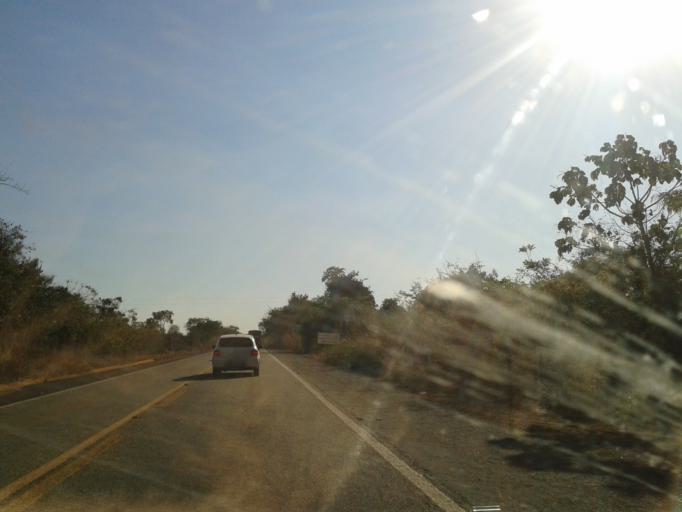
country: BR
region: Goias
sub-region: Mozarlandia
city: Mozarlandia
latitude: -15.0653
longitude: -50.6159
